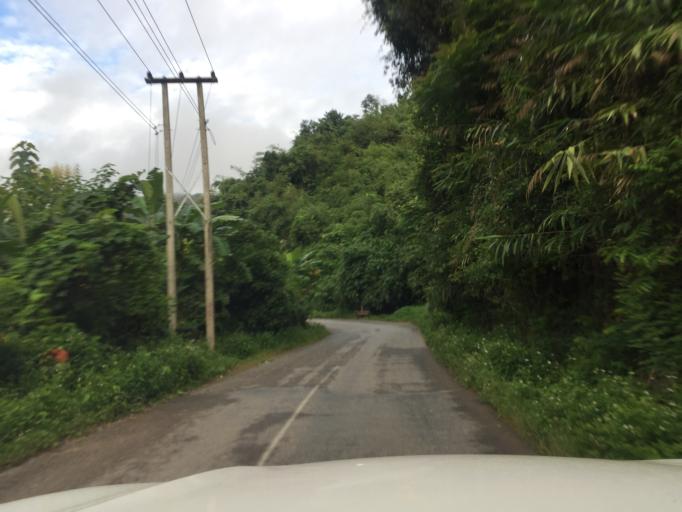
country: LA
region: Phongsali
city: Khoa
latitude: 21.1030
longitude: 102.2687
